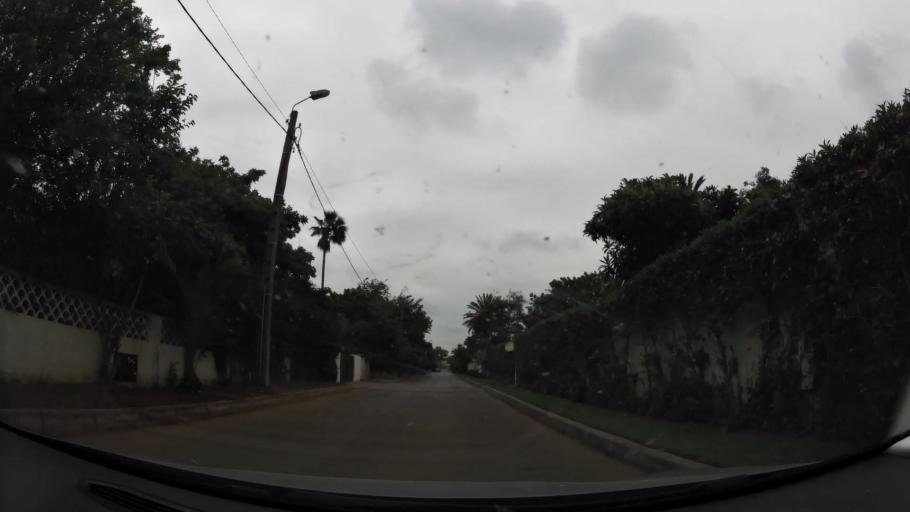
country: MA
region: Rabat-Sale-Zemmour-Zaer
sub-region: Rabat
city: Rabat
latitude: 33.9649
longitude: -6.8196
